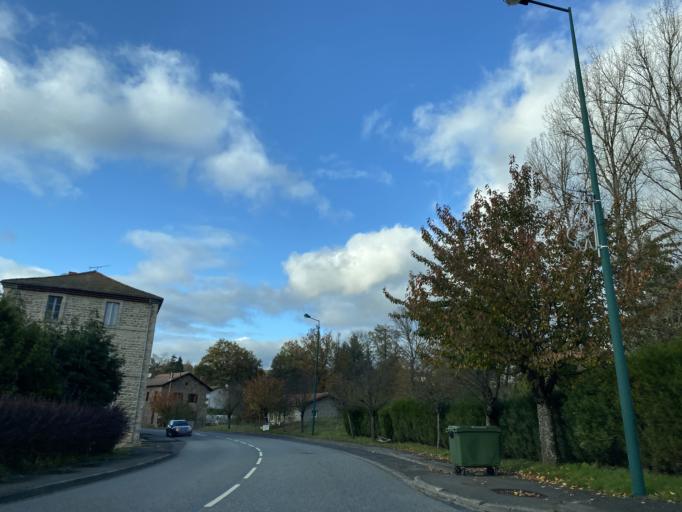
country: FR
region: Auvergne
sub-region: Departement du Puy-de-Dome
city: Job
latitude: 45.6434
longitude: 3.7061
